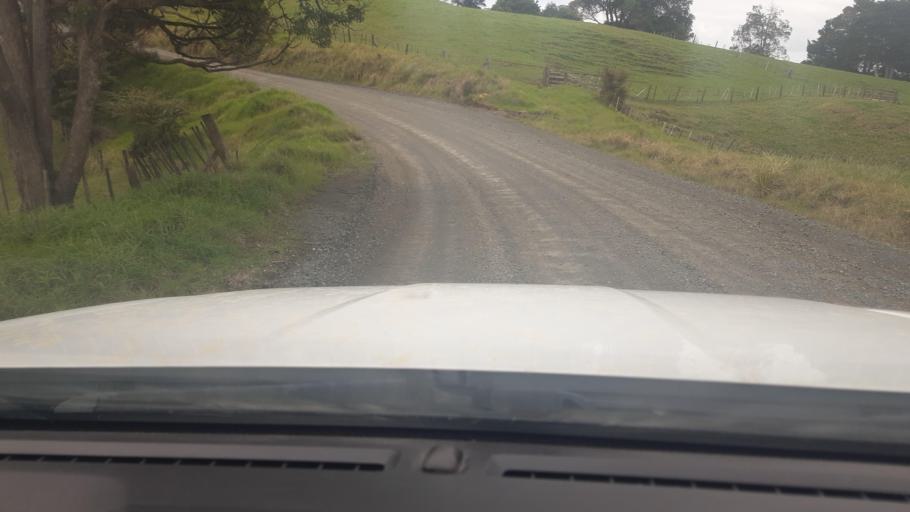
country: NZ
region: Northland
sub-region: Far North District
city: Kaitaia
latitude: -35.0906
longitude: 173.3174
